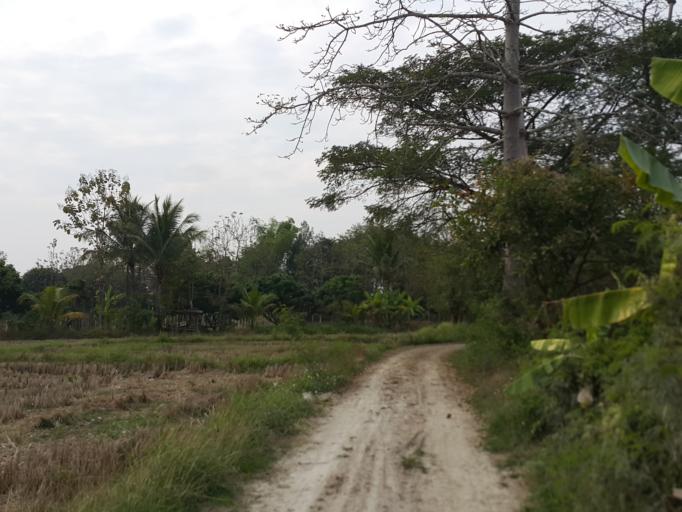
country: TH
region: Chiang Mai
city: San Kamphaeng
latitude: 18.7939
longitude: 99.1162
